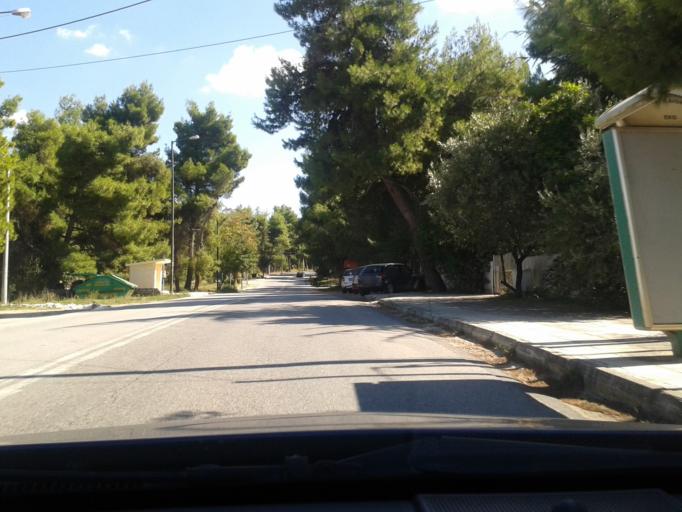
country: GR
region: Attica
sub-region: Nomarchia Anatolikis Attikis
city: Dionysos
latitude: 38.1042
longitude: 23.8719
